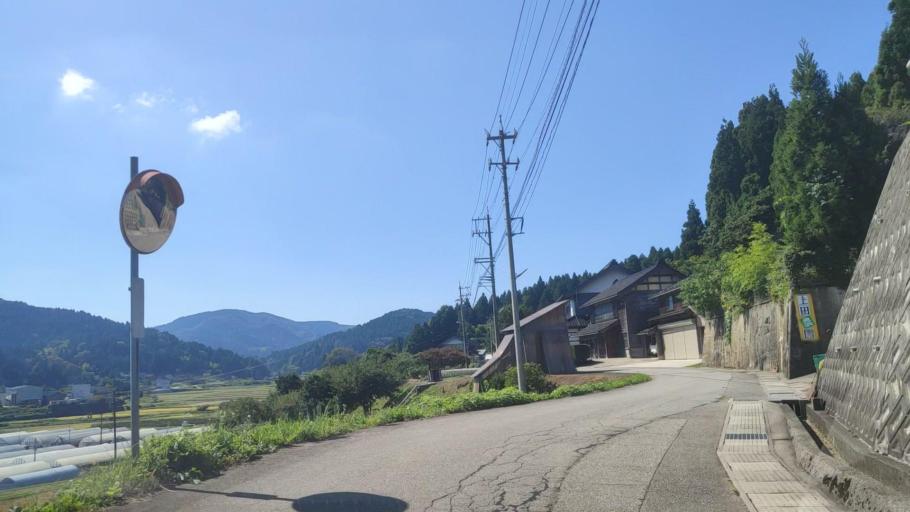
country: JP
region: Ishikawa
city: Nanao
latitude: 37.3703
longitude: 136.8697
